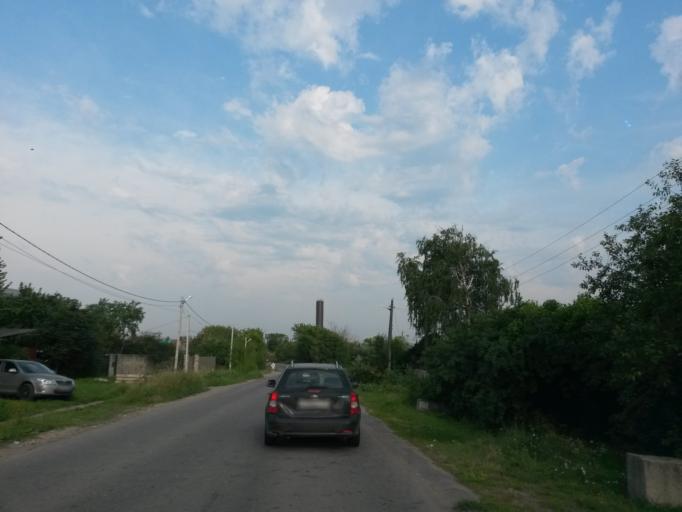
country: RU
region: Moskovskaya
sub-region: Podol'skiy Rayon
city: Podol'sk
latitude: 55.4466
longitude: 37.6271
